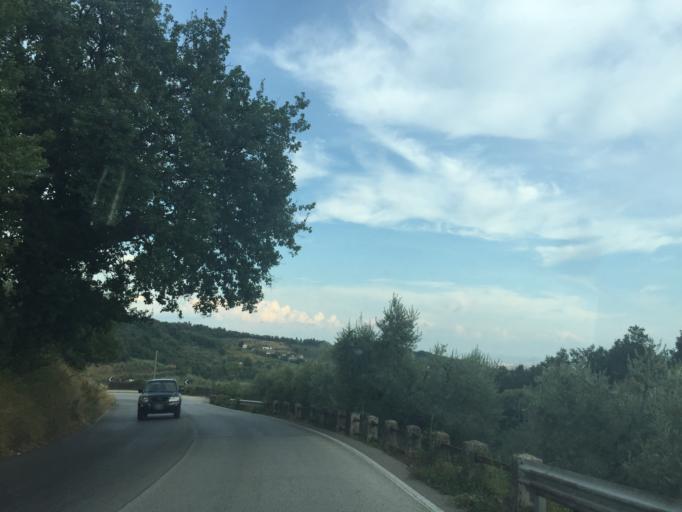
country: IT
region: Tuscany
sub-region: Provincia di Pistoia
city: Pistoia
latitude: 43.9720
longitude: 10.8858
